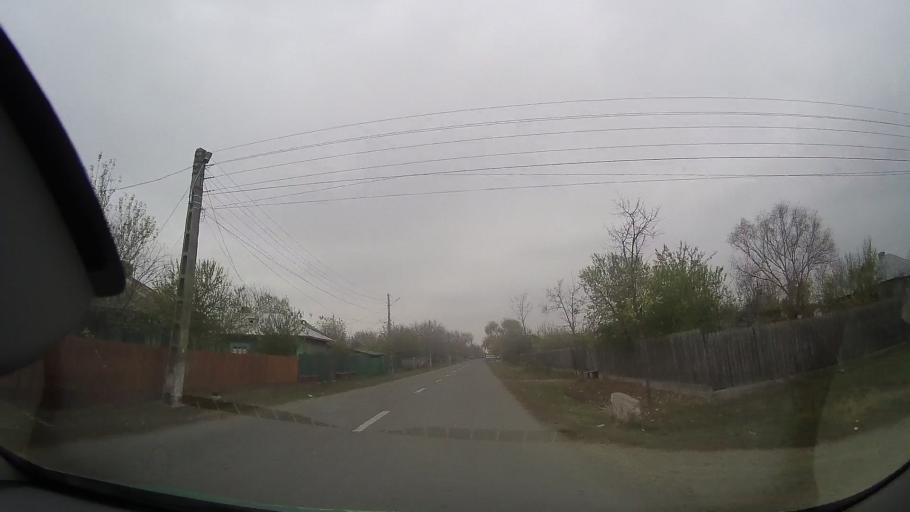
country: RO
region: Ialomita
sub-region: Comuna Grindu
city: Grindu
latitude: 44.7672
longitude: 26.9029
